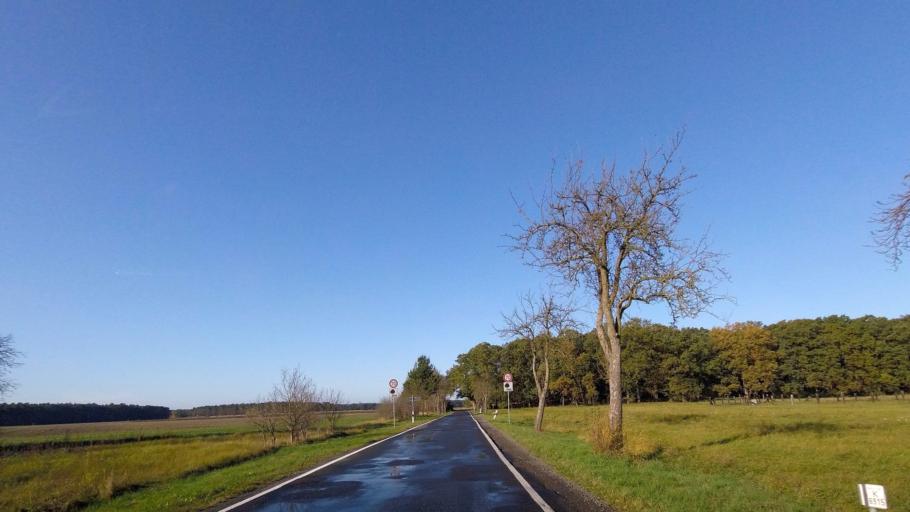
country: DE
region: Brandenburg
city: Treuenbrietzen
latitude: 52.1351
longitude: 12.9190
